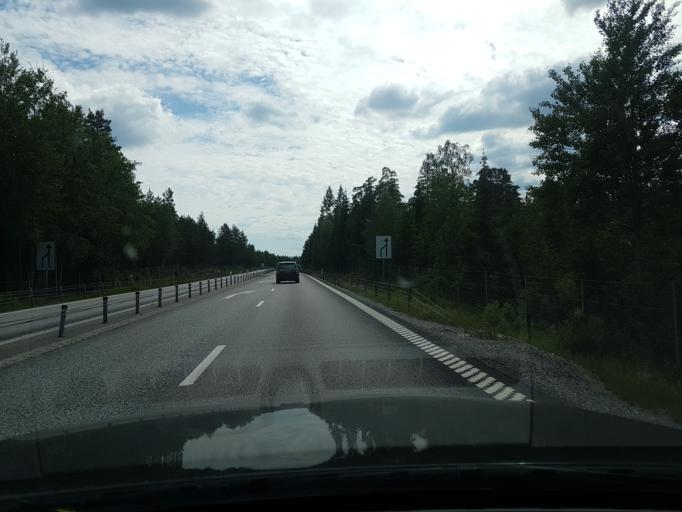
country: SE
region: Stockholm
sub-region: Osterakers Kommun
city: Akersberga
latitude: 59.6051
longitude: 18.2774
